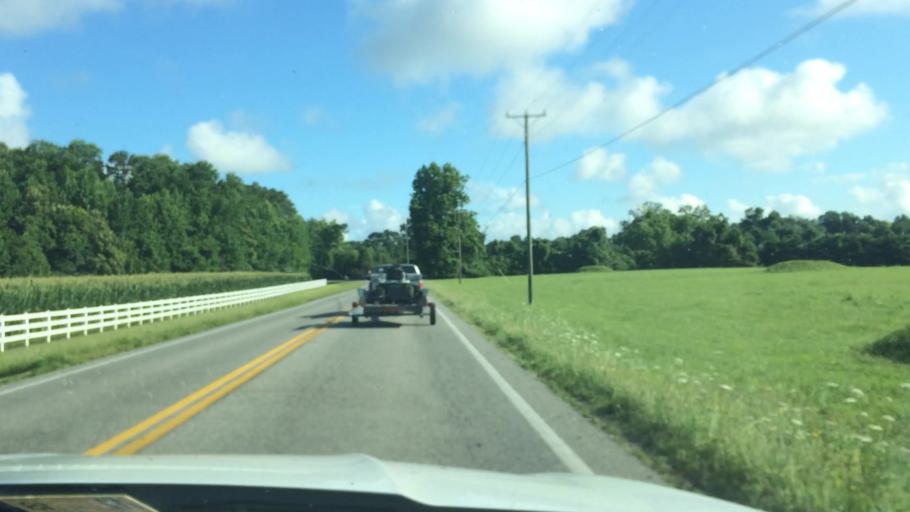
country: US
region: Virginia
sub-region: Middlesex County
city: Deltaville
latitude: 37.5329
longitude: -76.4219
